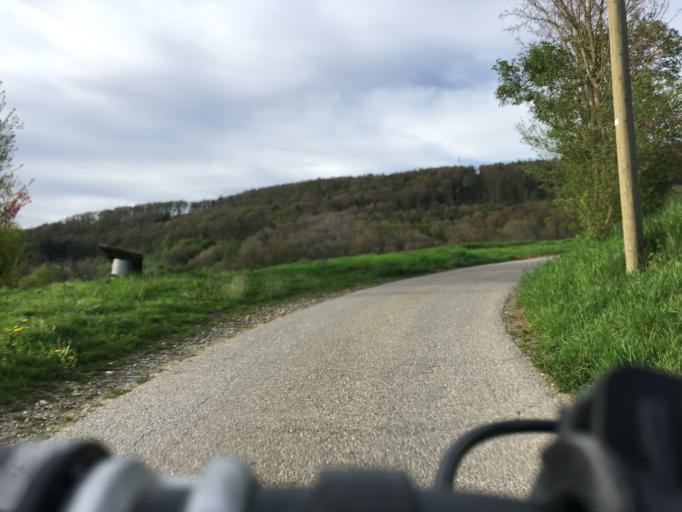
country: DE
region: Baden-Wuerttemberg
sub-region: Freiburg Region
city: Gottmadingen
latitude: 47.7385
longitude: 8.7654
